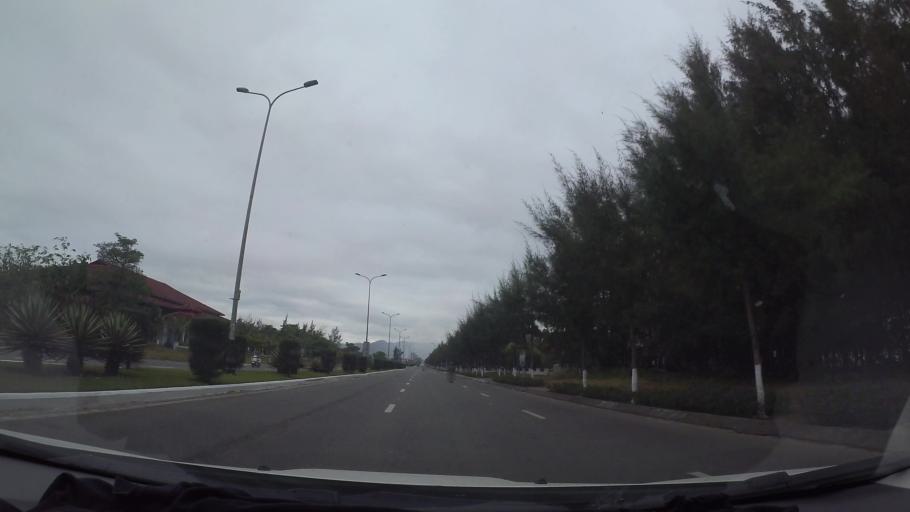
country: VN
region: Da Nang
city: Lien Chieu
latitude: 16.0943
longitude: 108.1470
